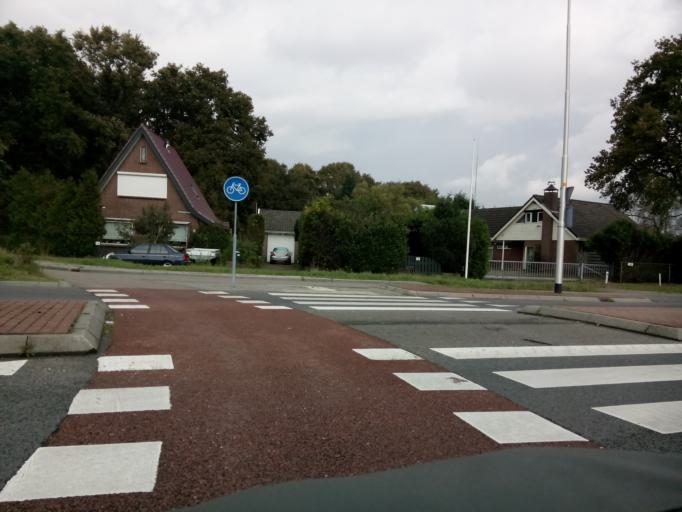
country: NL
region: Gelderland
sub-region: Gemeente Ermelo
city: Ermelo
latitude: 52.3198
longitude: 5.6241
